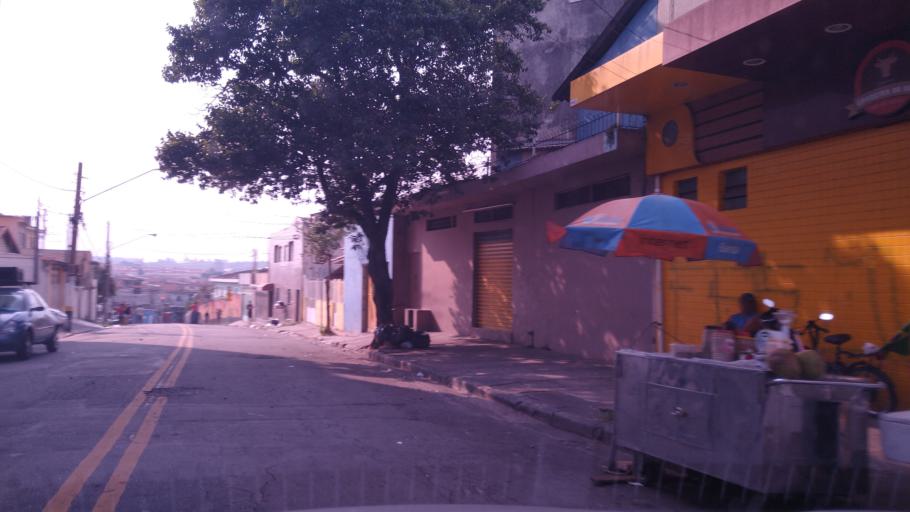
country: BR
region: Sao Paulo
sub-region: Osasco
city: Osasco
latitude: -23.5113
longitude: -46.7782
